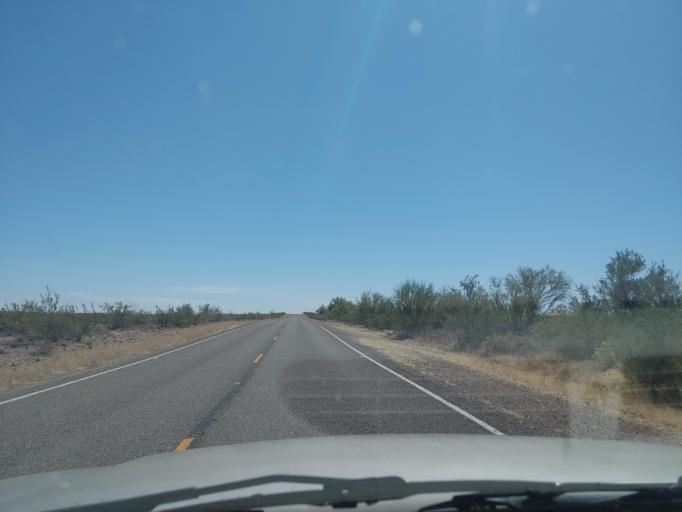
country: US
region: Arizona
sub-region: Maricopa County
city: Gila Bend
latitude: 32.8991
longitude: -113.2541
